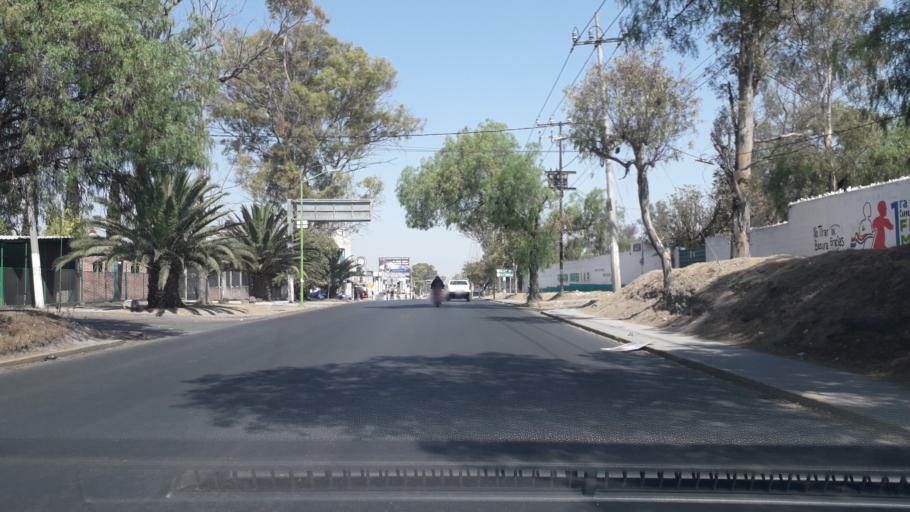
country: MX
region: Mexico
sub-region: Tecamac
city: Ojo de Agua
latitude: 19.6615
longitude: -99.0076
